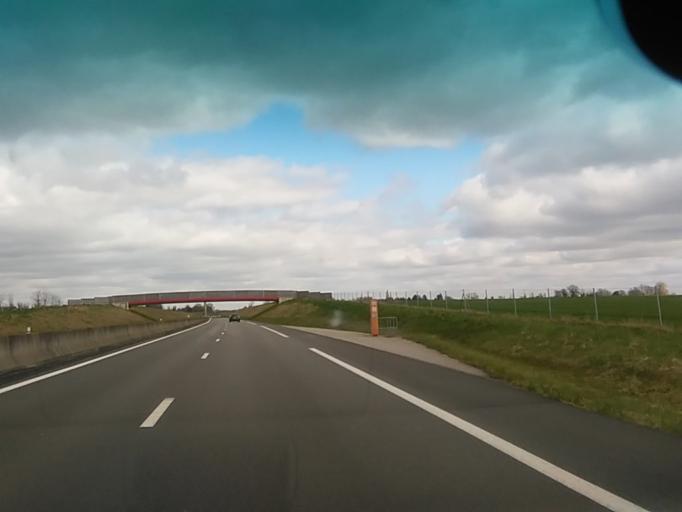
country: FR
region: Haute-Normandie
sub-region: Departement de l'Eure
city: Thiberville
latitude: 49.1007
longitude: 0.5055
